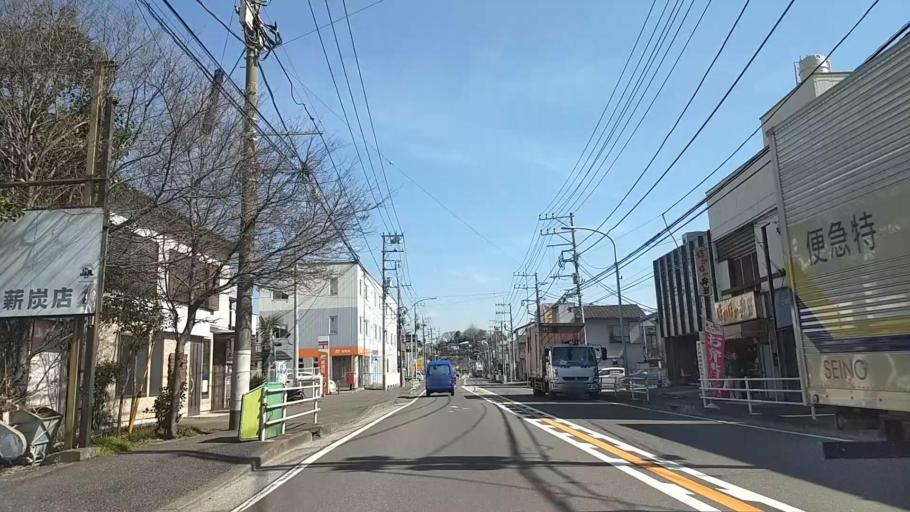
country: JP
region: Kanagawa
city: Kamakura
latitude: 35.3586
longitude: 139.5344
